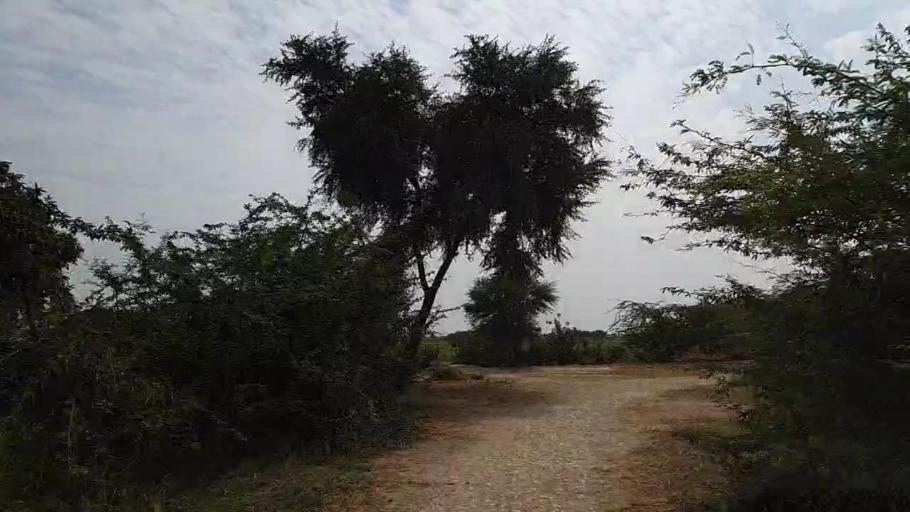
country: PK
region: Sindh
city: Daro Mehar
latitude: 24.8257
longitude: 68.1650
